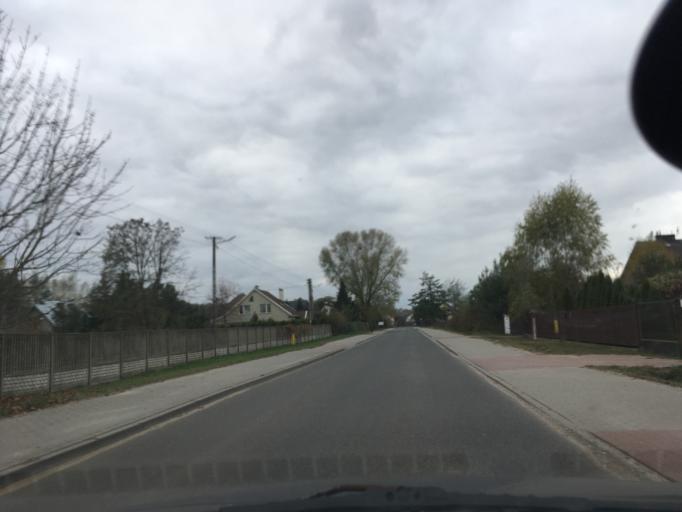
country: PL
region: Lodz Voivodeship
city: Zabia Wola
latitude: 52.0286
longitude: 20.6951
